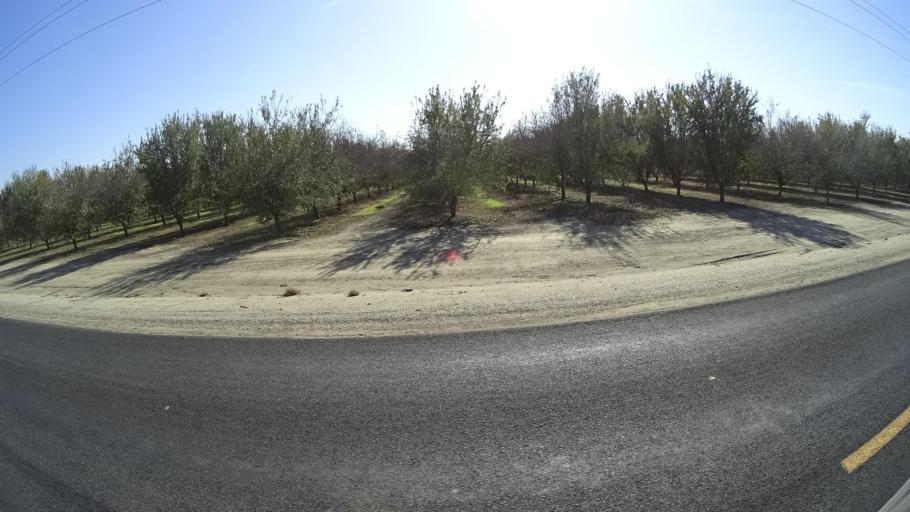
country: US
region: California
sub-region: Kern County
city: McFarland
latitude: 35.6454
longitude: -119.2515
